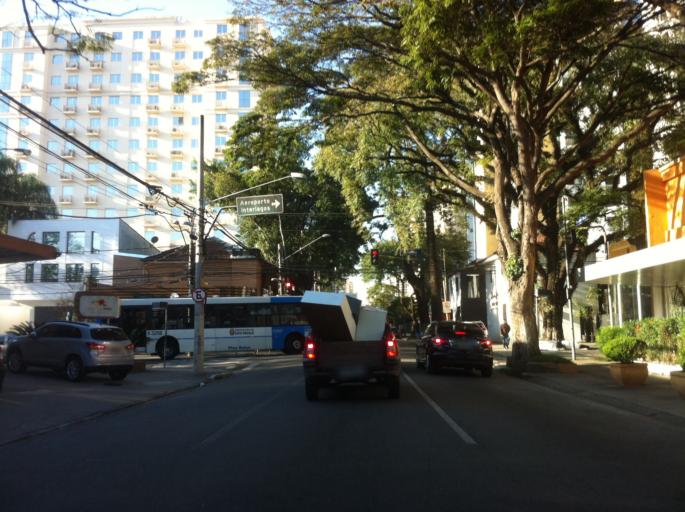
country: BR
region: Sao Paulo
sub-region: Sao Paulo
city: Sao Paulo
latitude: -23.6134
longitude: -46.6653
